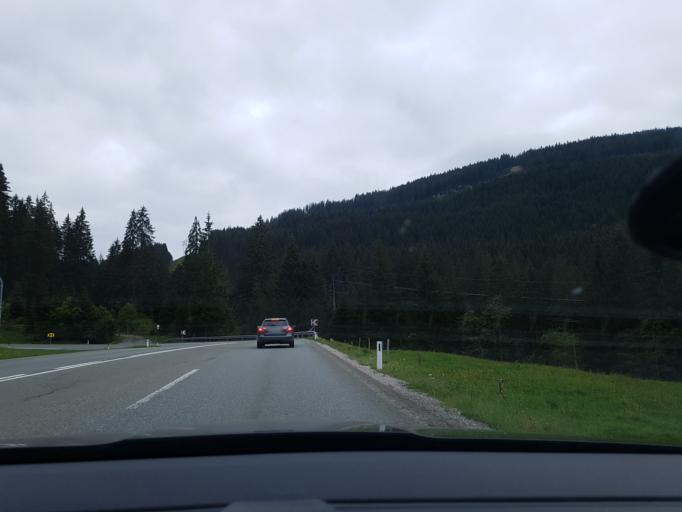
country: AT
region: Tyrol
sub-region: Politischer Bezirk Kitzbuhel
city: Jochberg
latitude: 47.3258
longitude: 12.4069
